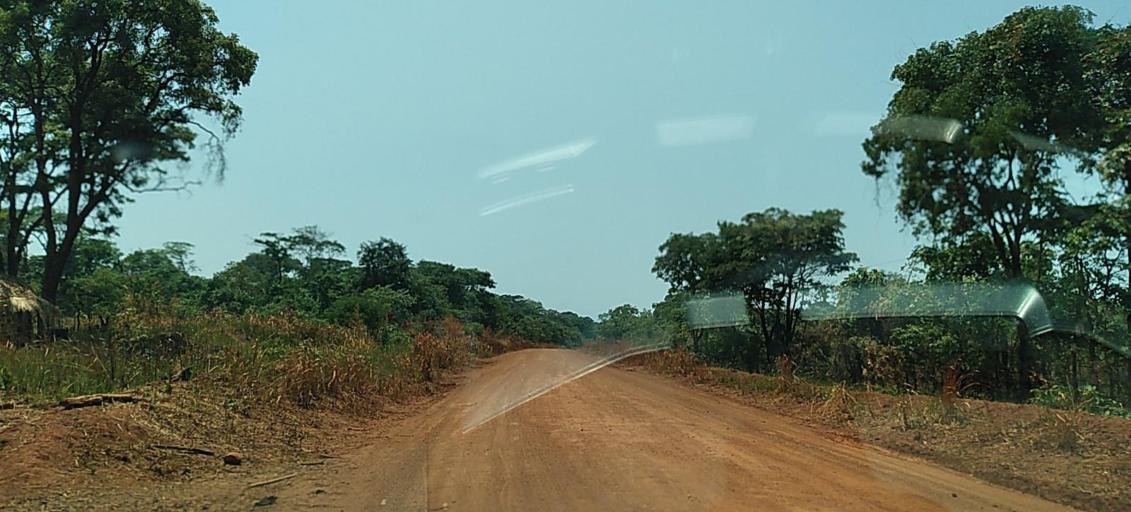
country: CD
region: Katanga
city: Kipushi
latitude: -11.9836
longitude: 26.8623
